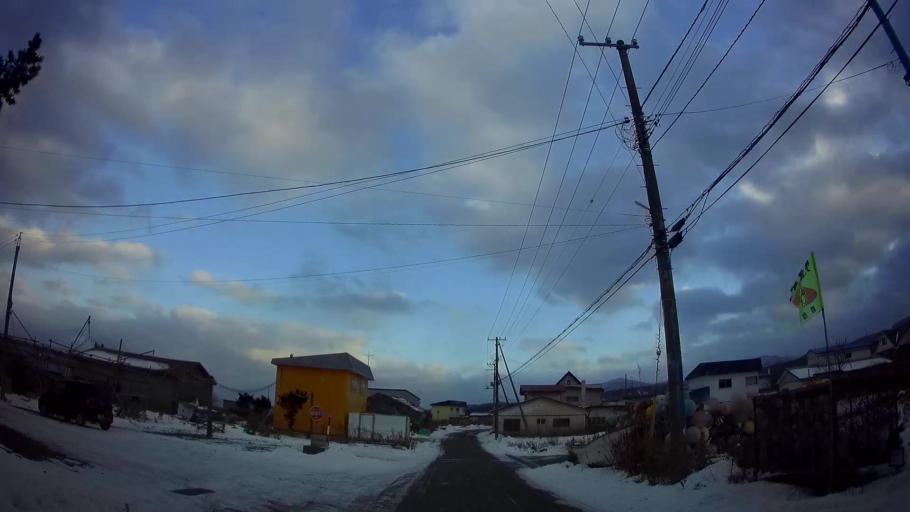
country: JP
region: Hokkaido
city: Nanae
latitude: 42.0393
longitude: 140.8178
